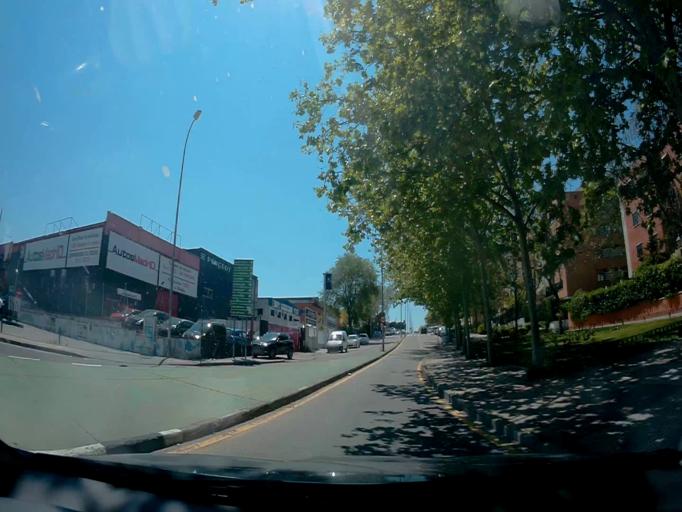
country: ES
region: Madrid
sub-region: Provincia de Madrid
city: Alcorcon
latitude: 40.3536
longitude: -3.7986
